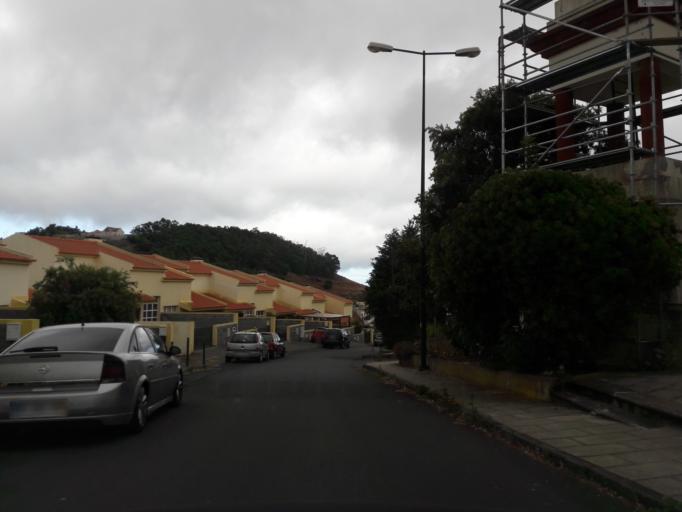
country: PT
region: Madeira
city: Canico
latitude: 32.6572
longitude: -16.8574
